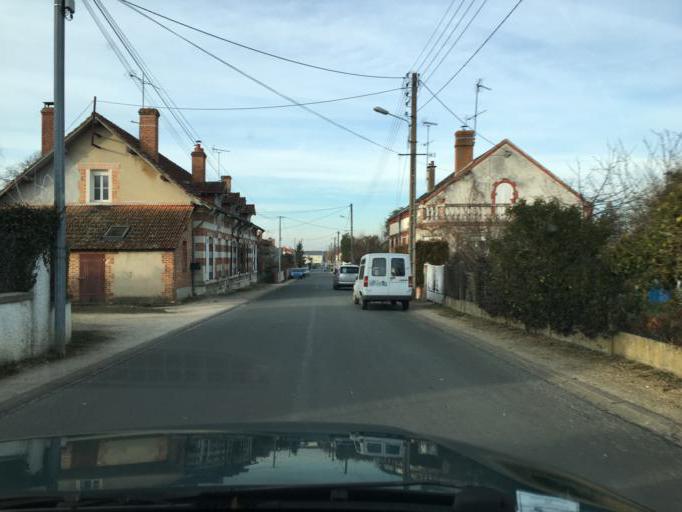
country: FR
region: Centre
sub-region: Departement du Loiret
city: La Ferte-Saint-Aubin
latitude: 47.7134
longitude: 1.9403
